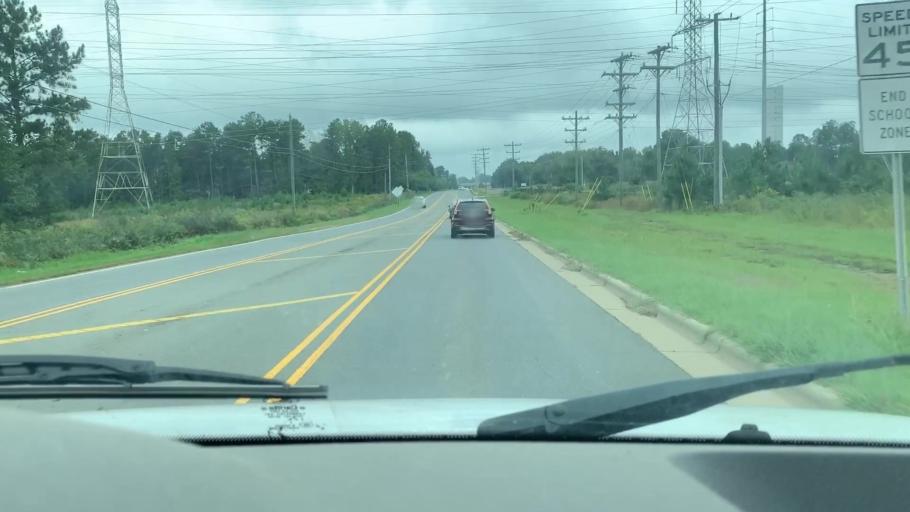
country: US
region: North Carolina
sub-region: Mecklenburg County
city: Huntersville
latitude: 35.3826
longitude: -80.8341
